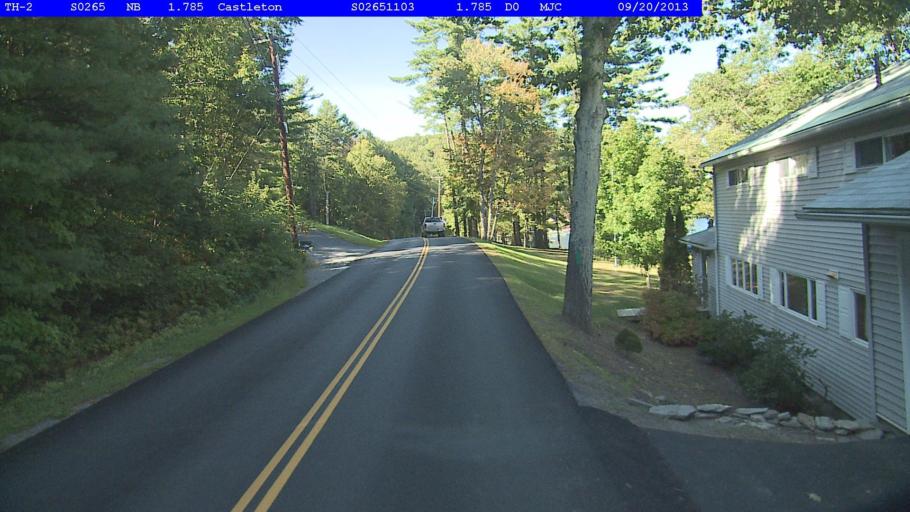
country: US
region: Vermont
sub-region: Rutland County
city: Fair Haven
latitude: 43.6283
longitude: -73.2331
